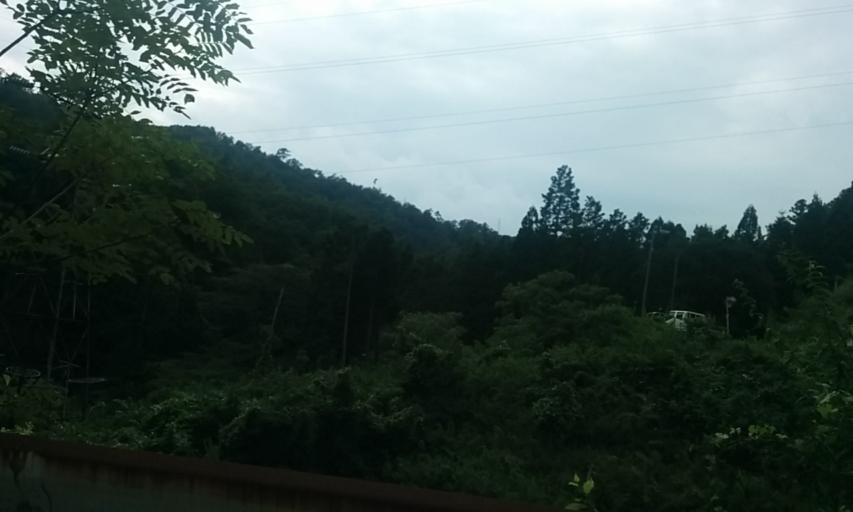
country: JP
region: Kyoto
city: Maizuru
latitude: 35.3531
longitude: 135.3451
